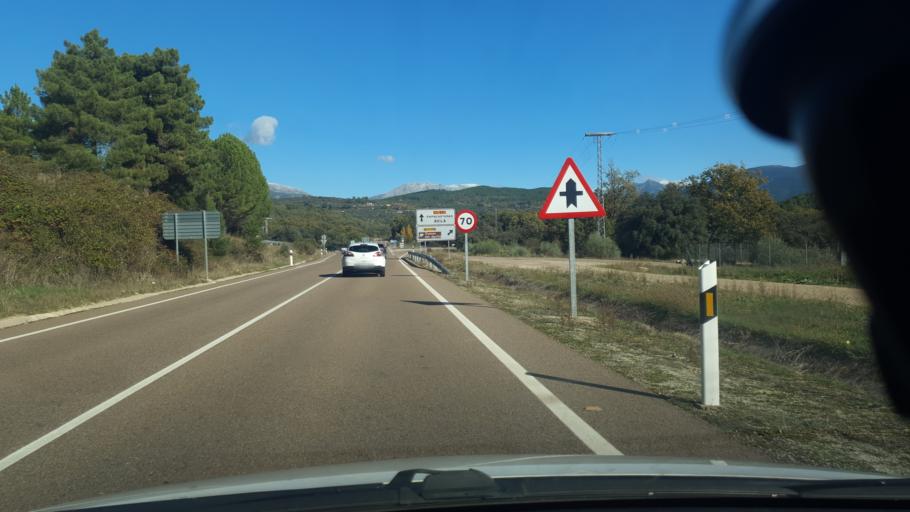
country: ES
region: Castille and Leon
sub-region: Provincia de Avila
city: Arenas de San Pedro
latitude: 40.1779
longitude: -5.0885
